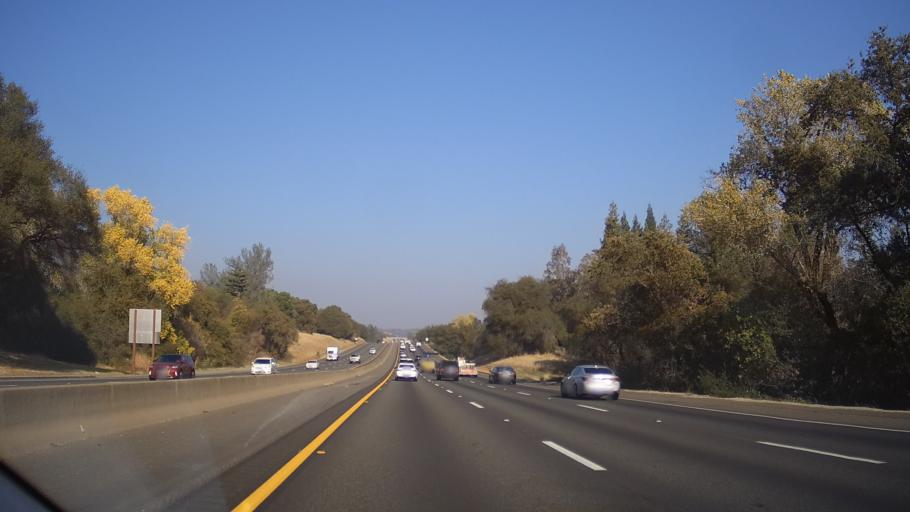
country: US
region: California
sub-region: Placer County
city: Loomis
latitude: 38.8412
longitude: -121.1598
